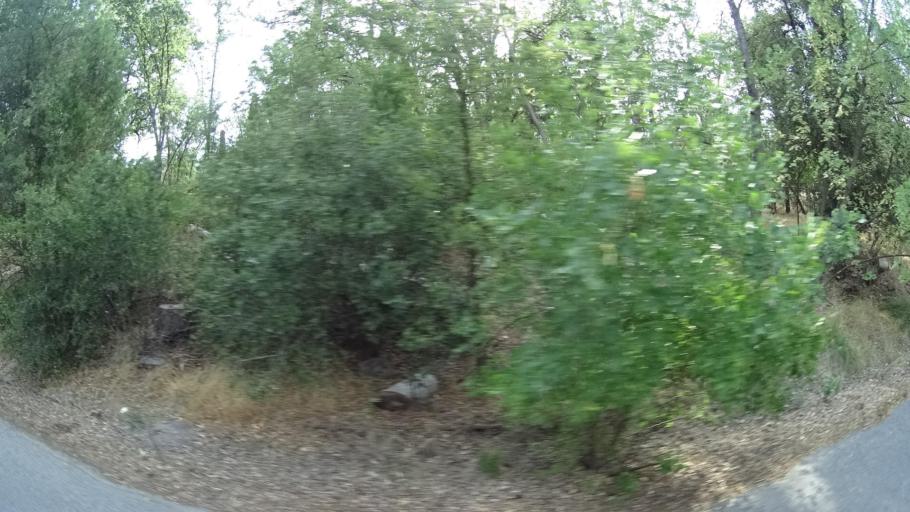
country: US
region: California
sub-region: Madera County
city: Ahwahnee
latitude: 37.4620
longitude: -119.7383
